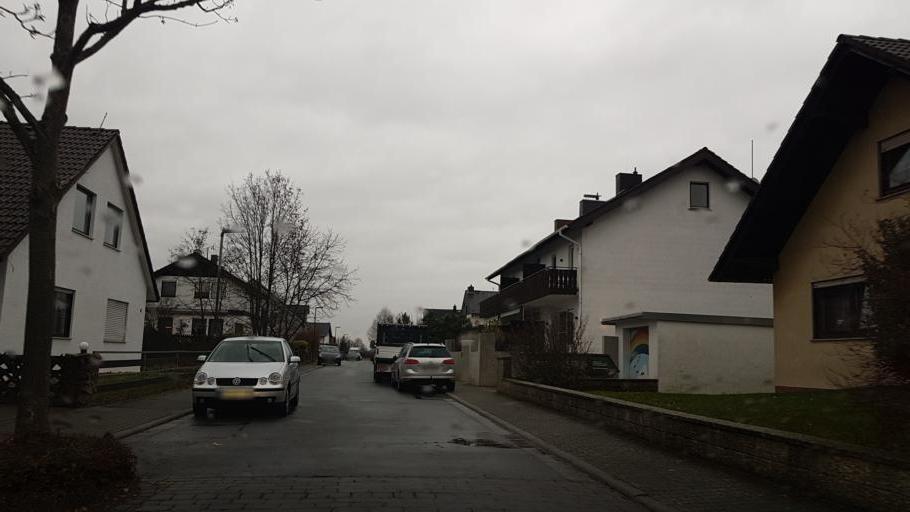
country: DE
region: Hesse
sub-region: Regierungsbezirk Darmstadt
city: Alsbach-Hahnlein
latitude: 49.7396
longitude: 8.5697
